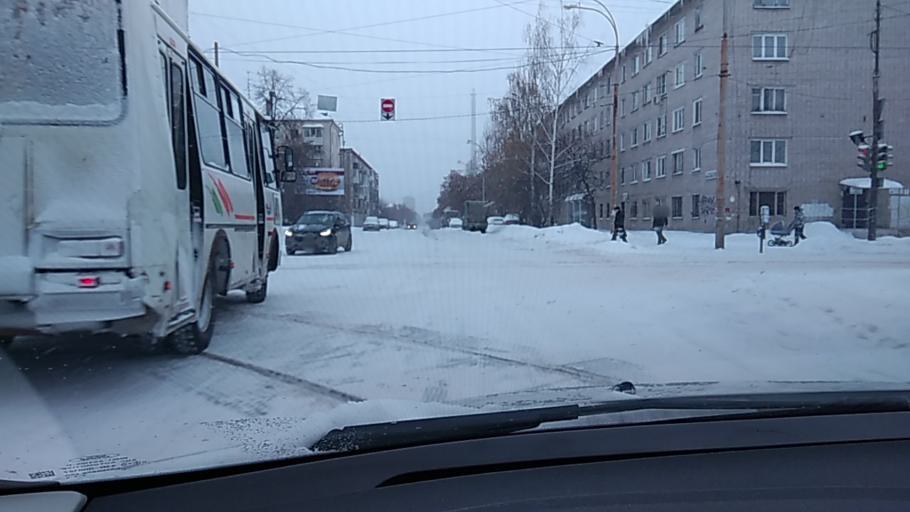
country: RU
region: Sverdlovsk
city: Yekaterinburg
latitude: 56.8134
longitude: 60.6115
